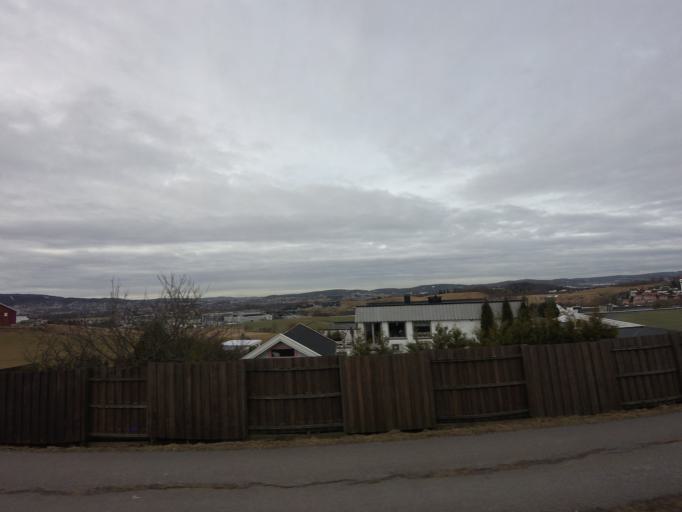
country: NO
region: Akershus
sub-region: Skedsmo
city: Lillestrom
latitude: 59.9815
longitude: 11.0524
